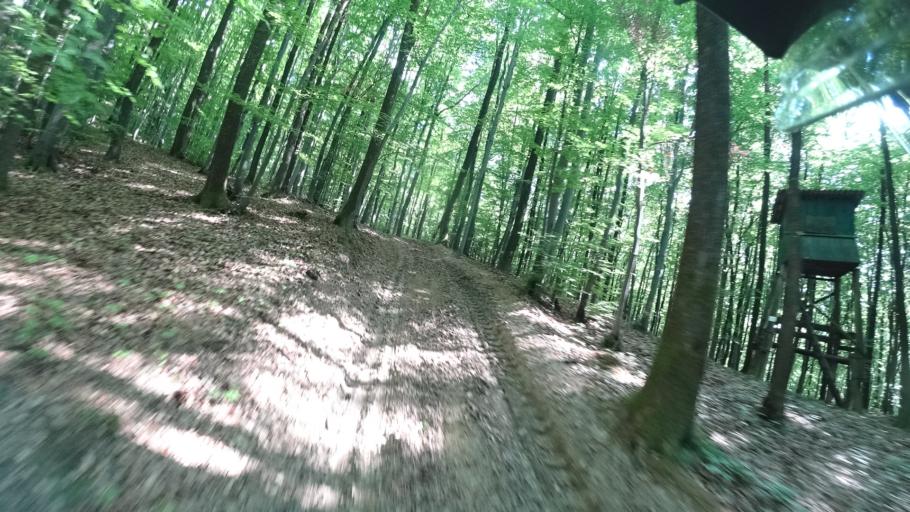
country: HR
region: Zagrebacka
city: Jablanovec
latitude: 45.8980
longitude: 15.8986
